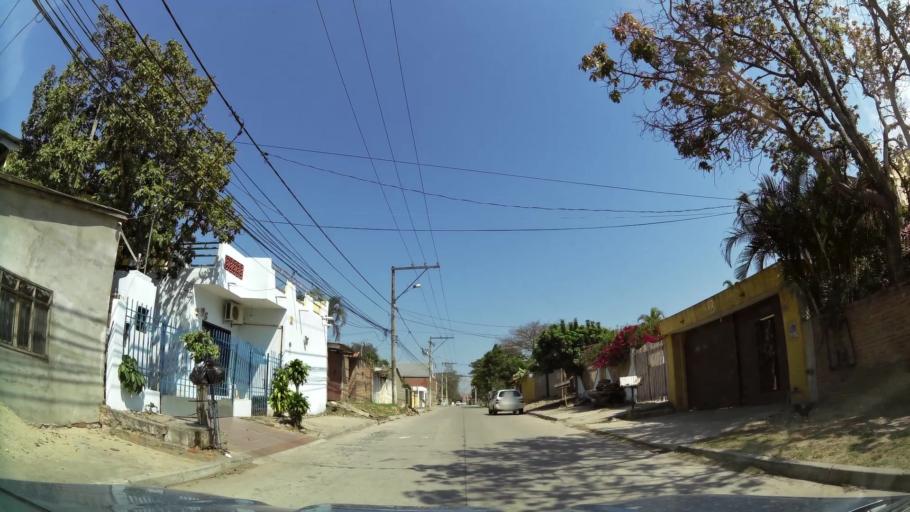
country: BO
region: Santa Cruz
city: Santa Cruz de la Sierra
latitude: -17.7526
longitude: -63.1959
